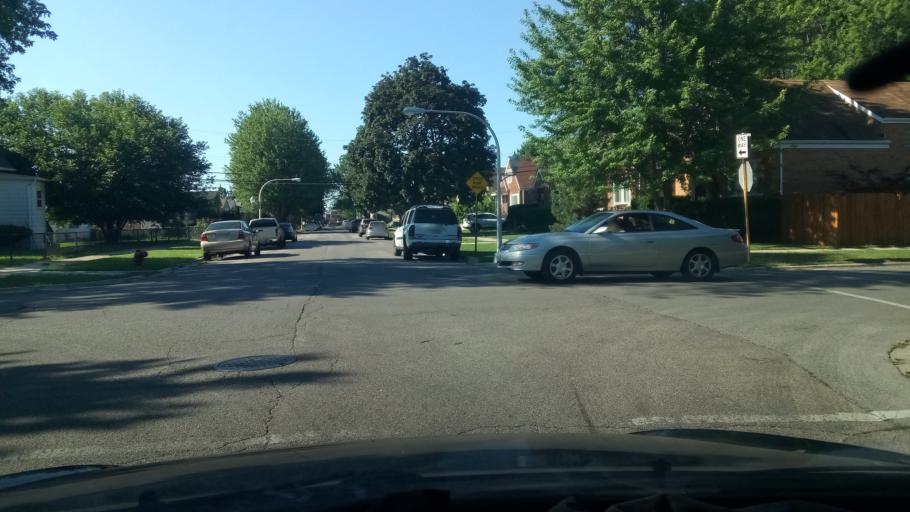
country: US
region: Illinois
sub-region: Cook County
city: Hometown
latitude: 41.7685
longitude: -87.7250
